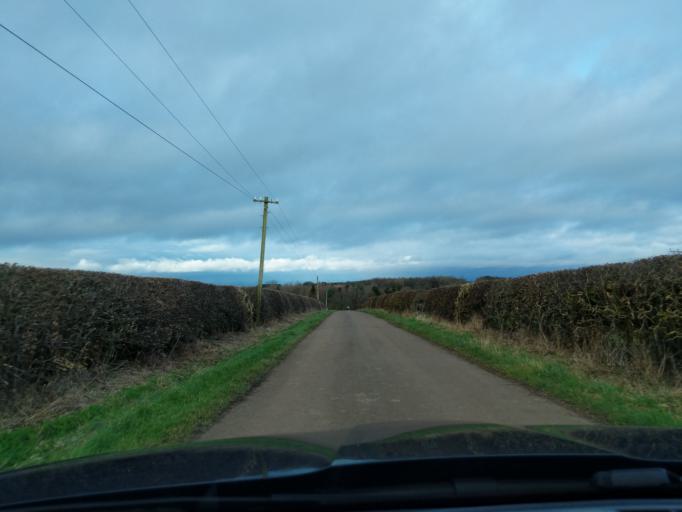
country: GB
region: England
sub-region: Northumberland
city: Ancroft
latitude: 55.6932
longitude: -1.9747
